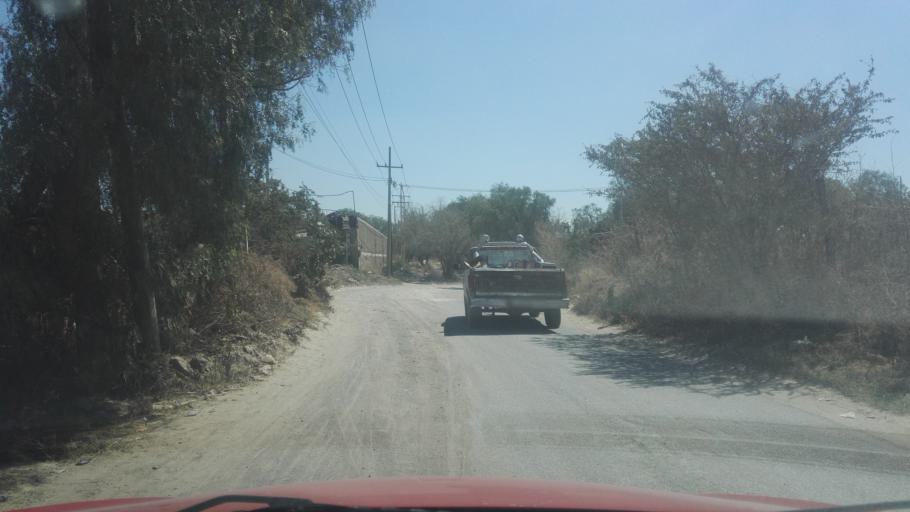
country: MX
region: Guanajuato
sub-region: Leon
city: Fraccionamiento Paraiso Real
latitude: 21.0871
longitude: -101.5910
